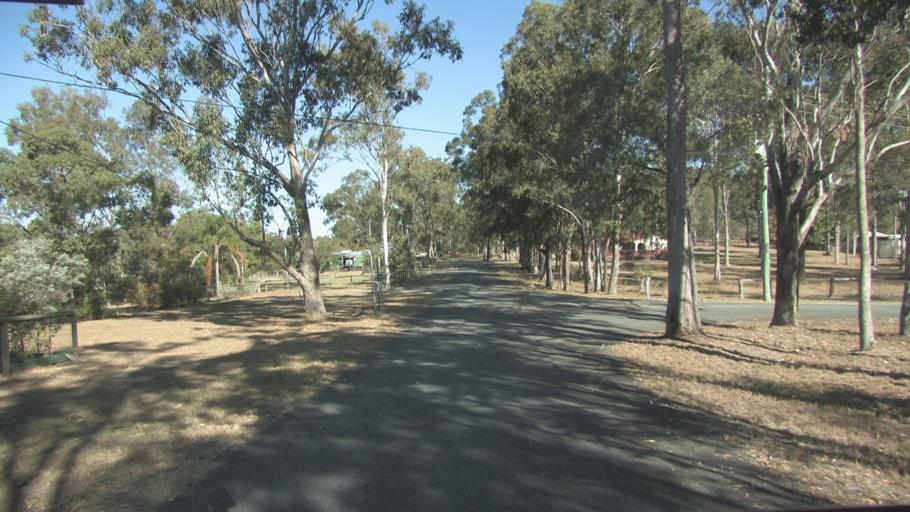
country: AU
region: Queensland
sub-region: Logan
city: Cedar Vale
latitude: -27.8575
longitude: 153.0317
